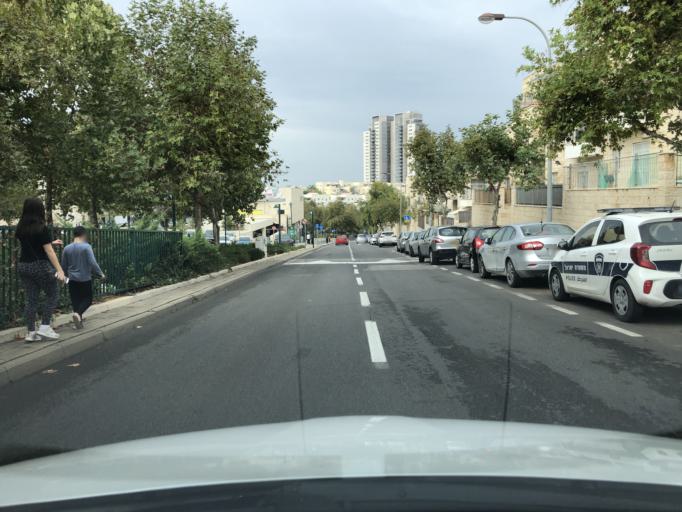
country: IL
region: Central District
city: Modiin
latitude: 31.9138
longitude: 35.0075
